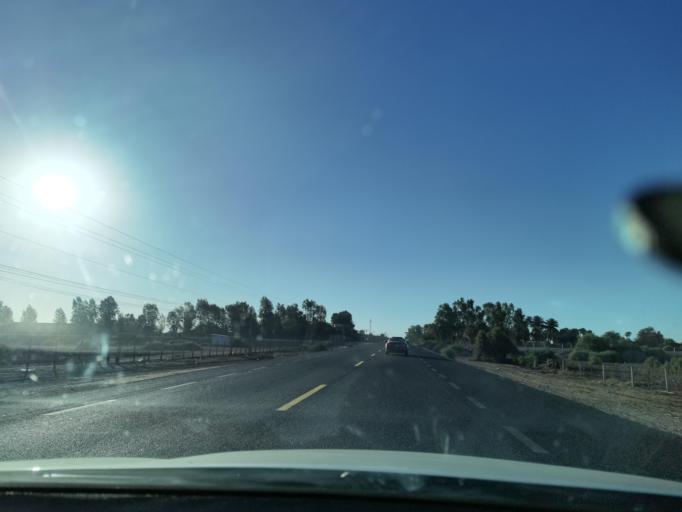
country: MX
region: Baja California
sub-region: Mexicali
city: Islas Agrarias Grupo A
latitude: 32.6428
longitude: -115.3092
